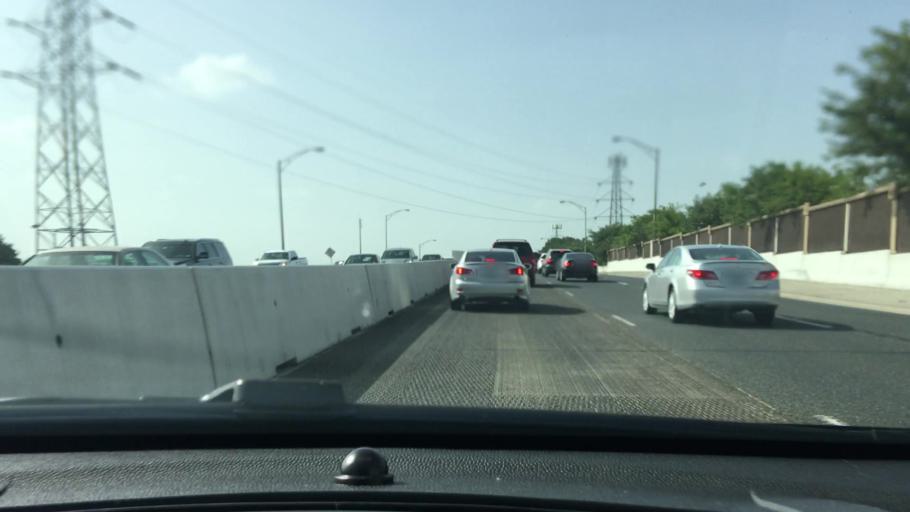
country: US
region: Texas
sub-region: Dallas County
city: Addison
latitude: 32.9083
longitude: -96.8141
